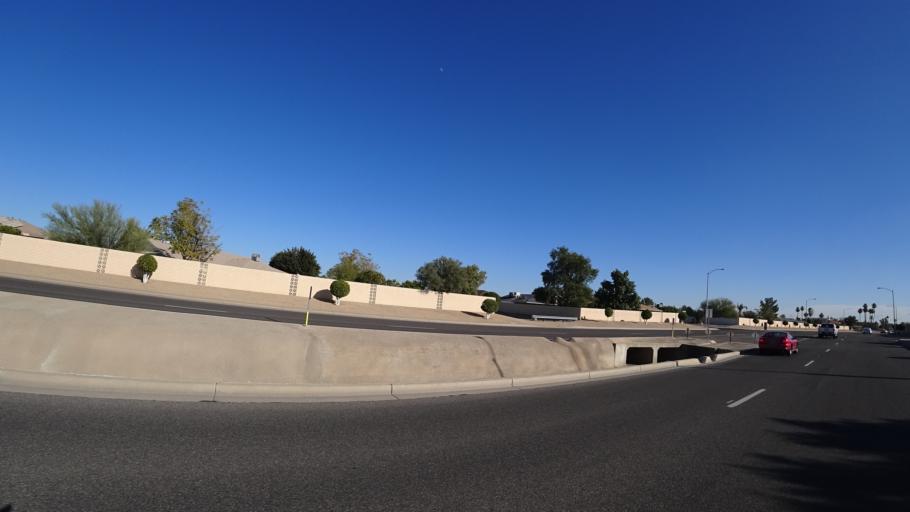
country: US
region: Arizona
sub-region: Maricopa County
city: Sun City West
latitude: 33.6690
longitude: -112.3328
